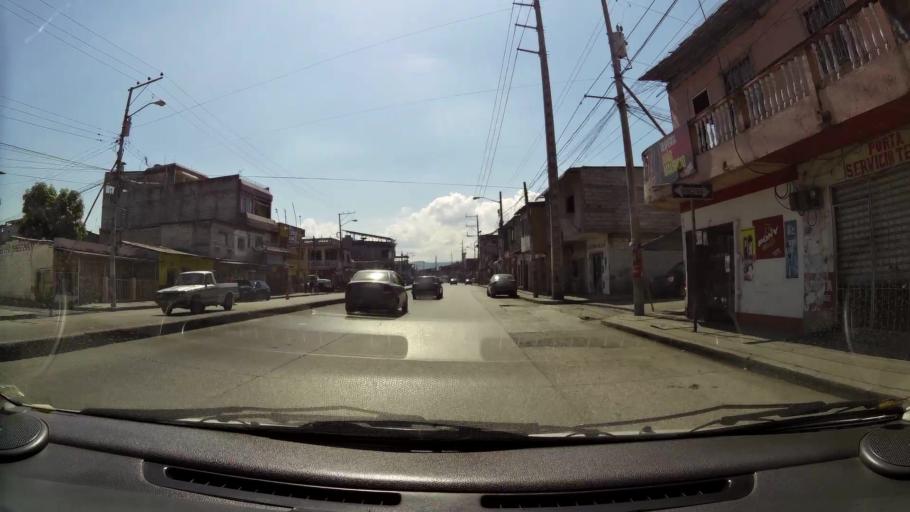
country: EC
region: Guayas
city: Guayaquil
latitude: -2.2301
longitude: -79.9405
